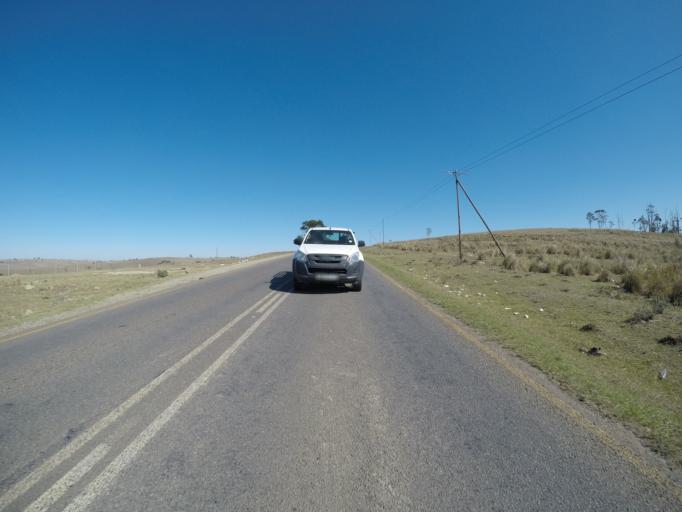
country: ZA
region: Eastern Cape
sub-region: OR Tambo District Municipality
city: Mthatha
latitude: -31.8058
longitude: 28.7554
